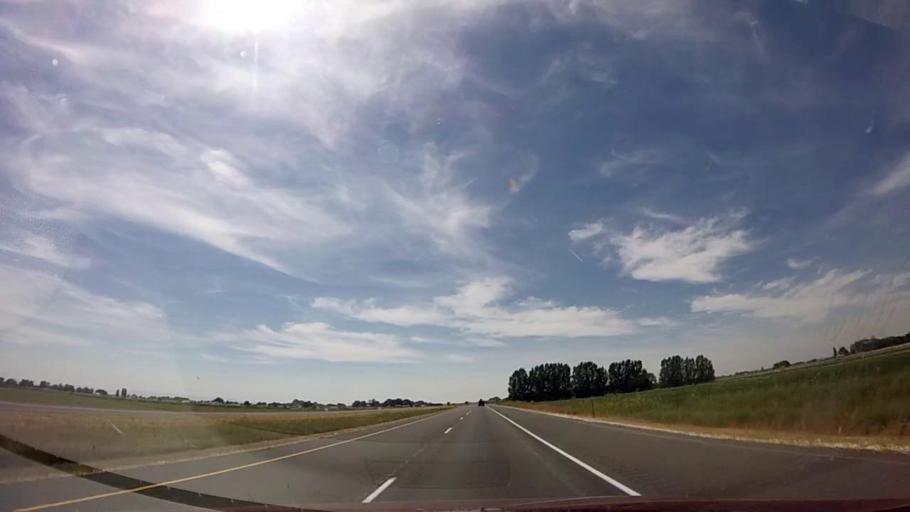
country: US
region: Idaho
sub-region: Minidoka County
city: Rupert
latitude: 42.5690
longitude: -113.6802
